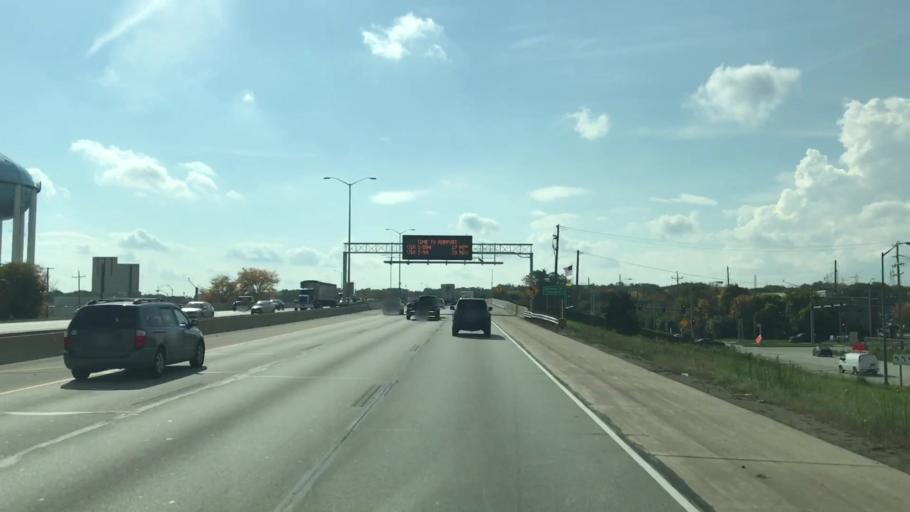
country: US
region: Wisconsin
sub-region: Waukesha County
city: Butler
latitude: 43.0758
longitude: -88.0584
